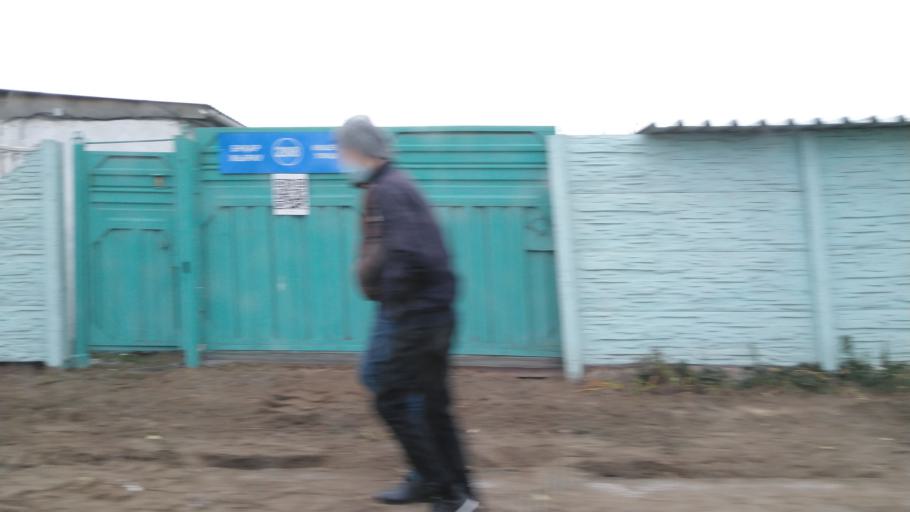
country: KZ
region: Pavlodar
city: Pavlodar
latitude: 52.2755
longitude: 76.9571
